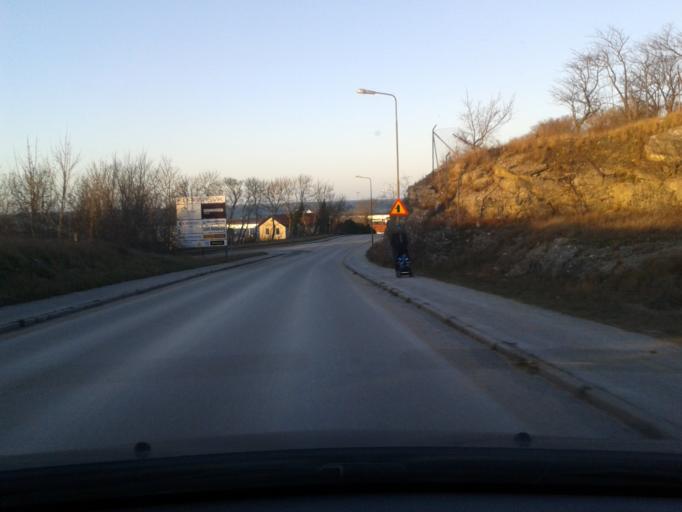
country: SE
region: Gotland
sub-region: Gotland
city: Visby
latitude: 57.6288
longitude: 18.2806
